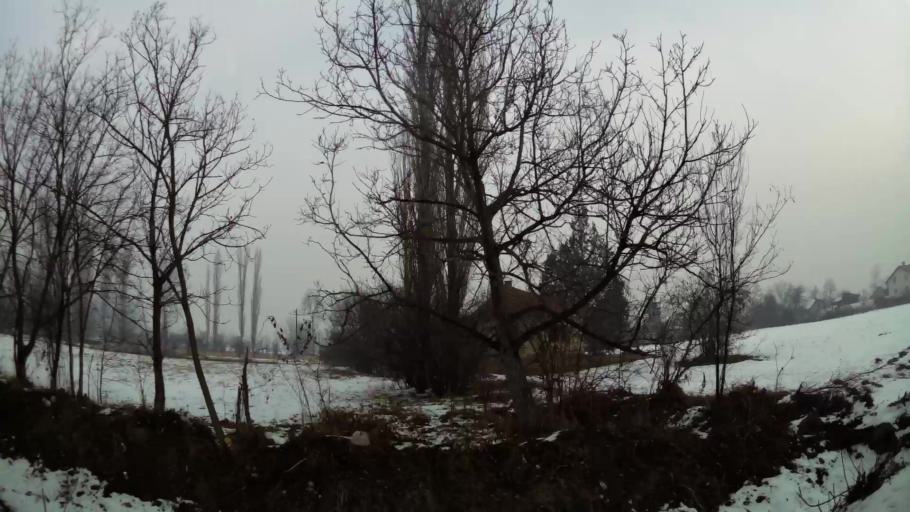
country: MK
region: Ilinden
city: Idrizovo
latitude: 41.9634
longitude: 21.5734
